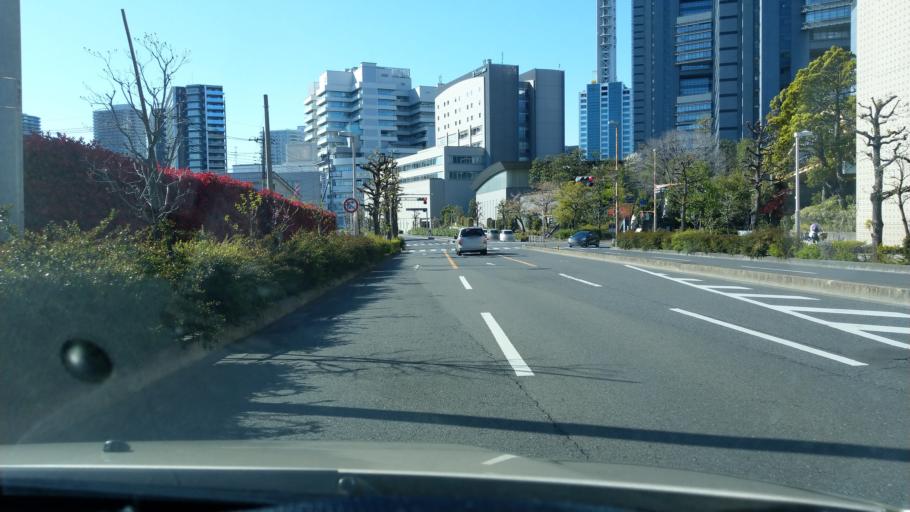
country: JP
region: Saitama
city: Yono
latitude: 35.8890
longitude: 139.6347
